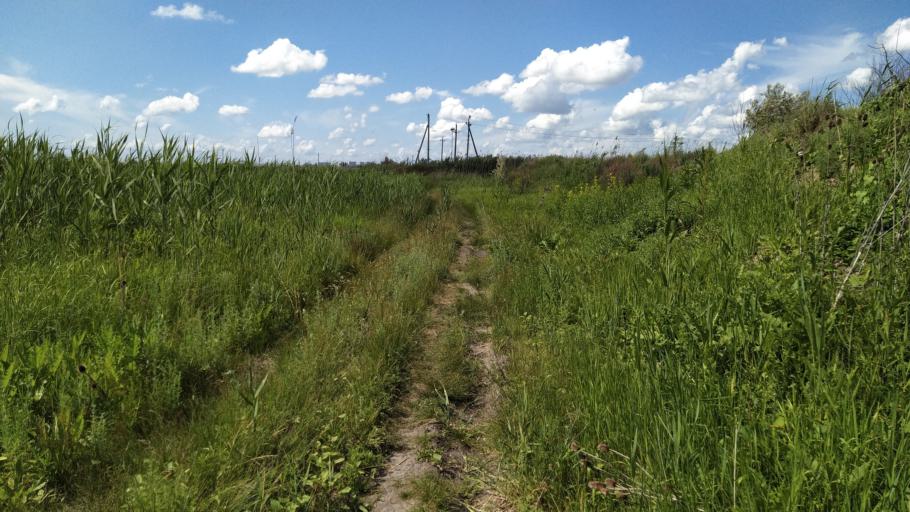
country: RU
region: Rostov
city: Bataysk
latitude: 47.1402
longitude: 39.6691
